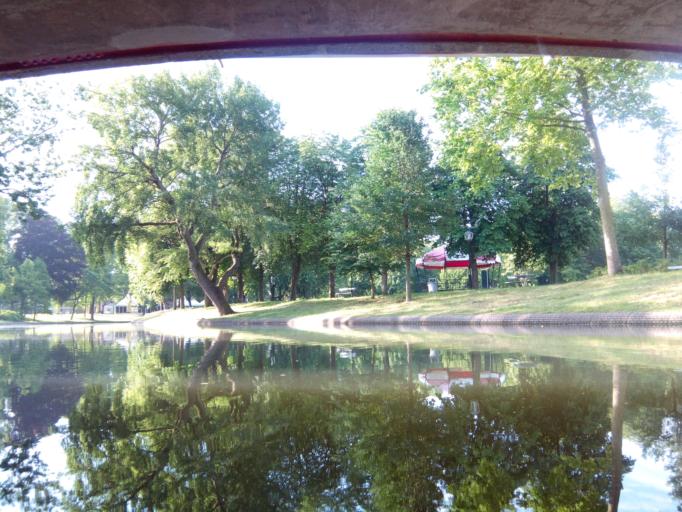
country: NL
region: Utrecht
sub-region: Gemeente Utrecht
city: Utrecht
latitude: 52.0902
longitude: 5.1278
